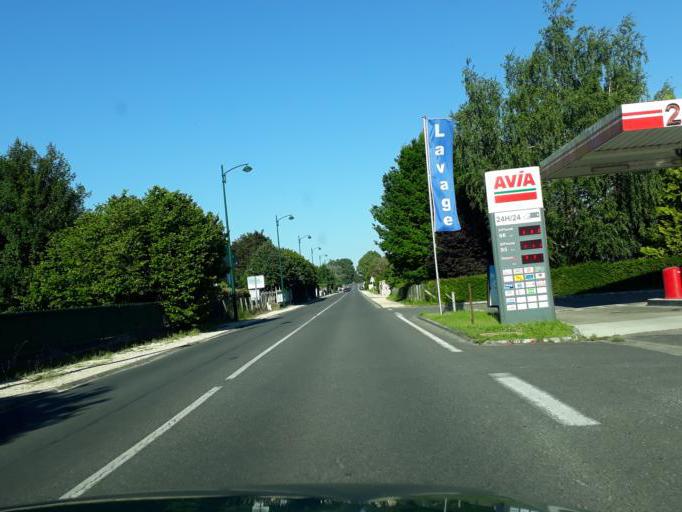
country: FR
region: Centre
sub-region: Departement du Cher
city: Boulleret
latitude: 47.4109
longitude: 2.8961
